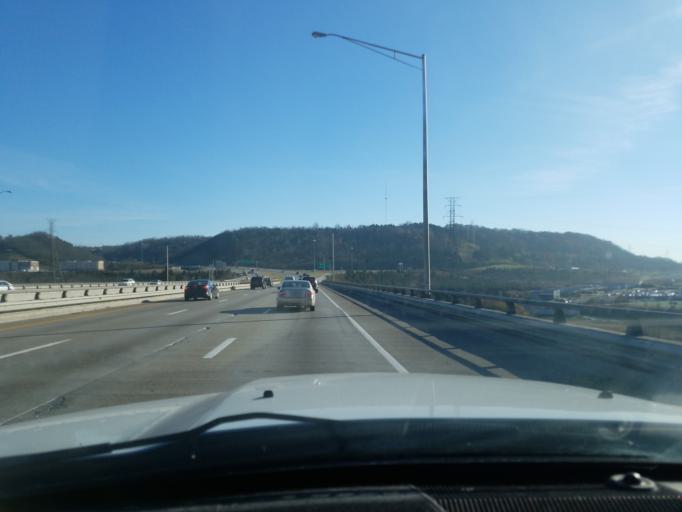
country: US
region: Kentucky
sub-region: Kenton County
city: Taylor Mill
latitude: 39.0226
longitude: -84.4892
